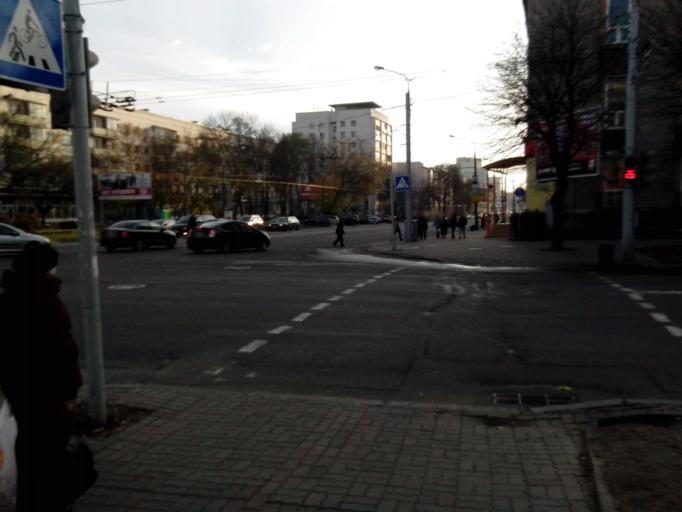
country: BY
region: Minsk
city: Minsk
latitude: 53.9214
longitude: 27.5675
